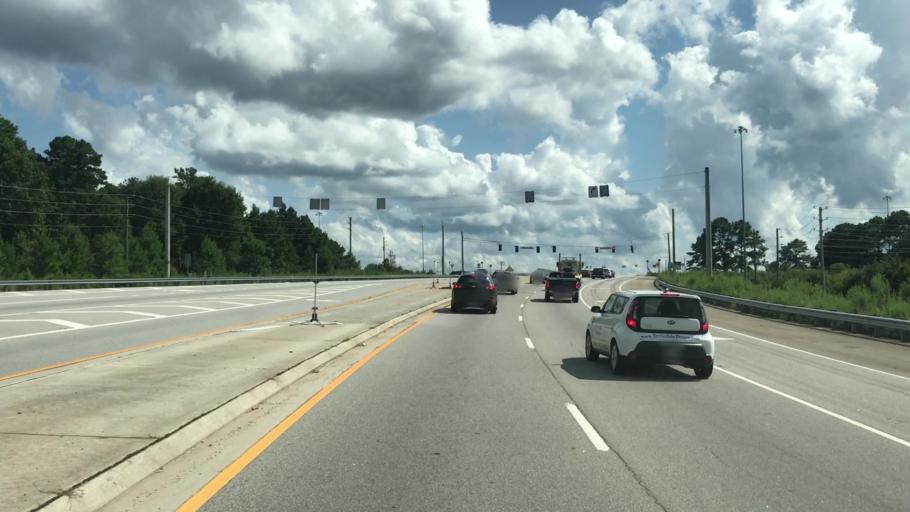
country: US
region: Georgia
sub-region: Newton County
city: Covington
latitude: 33.6155
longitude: -83.8238
